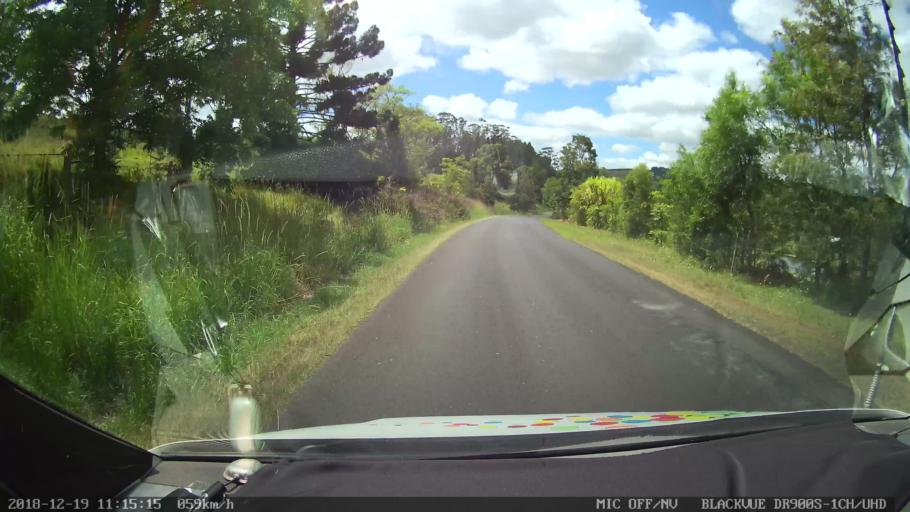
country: AU
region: New South Wales
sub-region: Lismore Municipality
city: Nimbin
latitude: -28.6663
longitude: 153.2771
